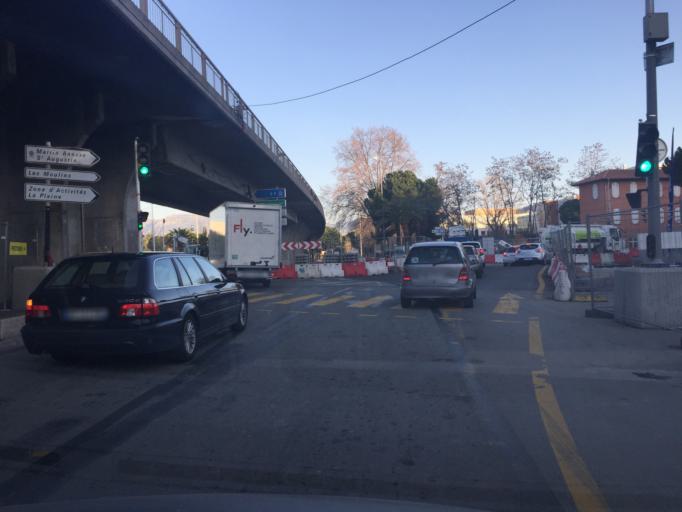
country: FR
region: Provence-Alpes-Cote d'Azur
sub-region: Departement des Alpes-Maritimes
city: Saint-Laurent-du-Var
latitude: 43.6764
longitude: 7.2014
